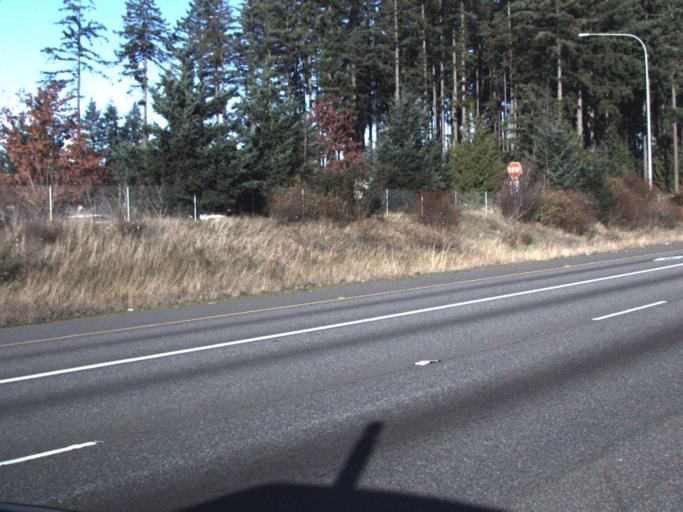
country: US
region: Washington
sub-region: Snohomish County
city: Mill Creek
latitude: 47.9001
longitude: -122.2129
